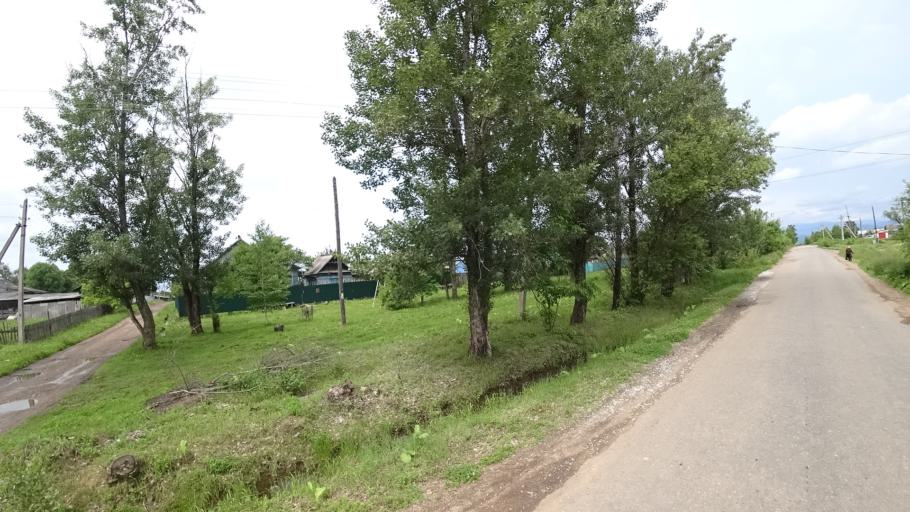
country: RU
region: Primorskiy
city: Novosysoyevka
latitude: 44.2312
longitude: 133.3605
